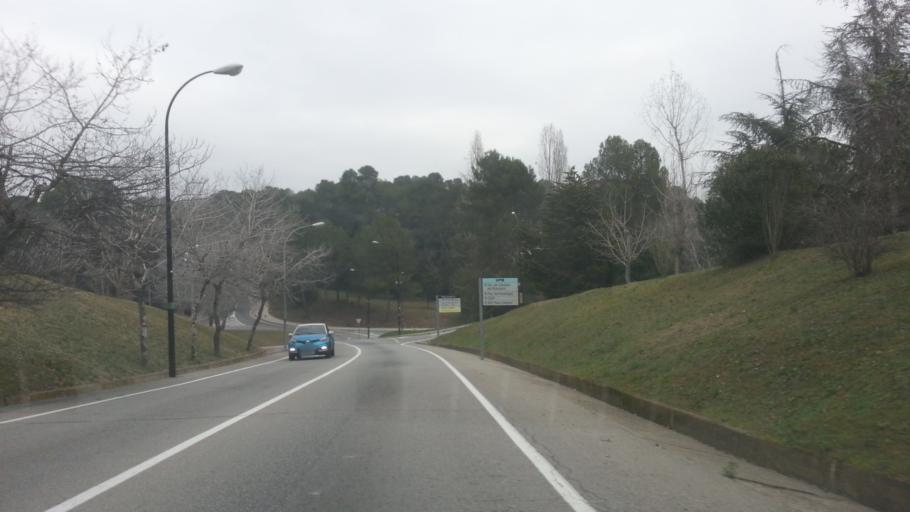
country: ES
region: Catalonia
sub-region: Provincia de Barcelona
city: Barbera del Valles
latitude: 41.5045
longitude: 2.1003
